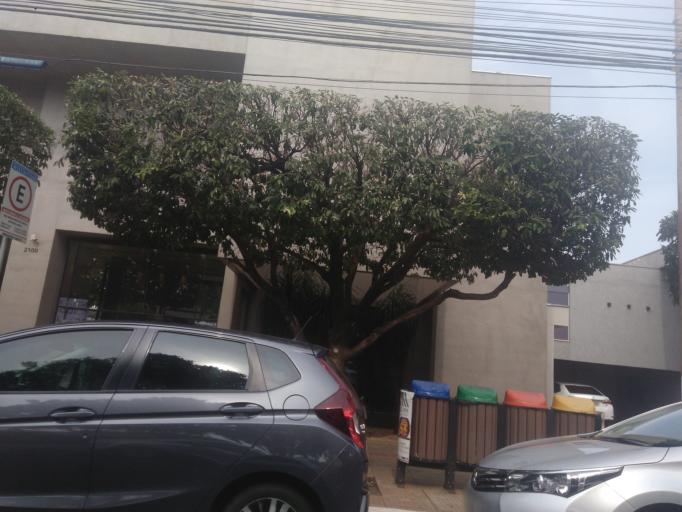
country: BR
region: Mato Grosso do Sul
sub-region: Dourados
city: Dourados
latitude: -22.2265
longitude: -54.8098
